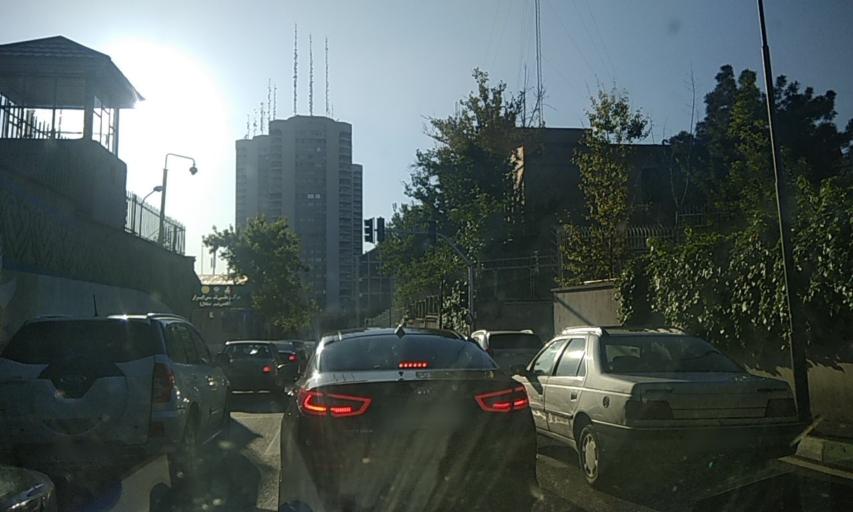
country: IR
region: Tehran
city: Tajrish
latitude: 35.7641
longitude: 51.4075
